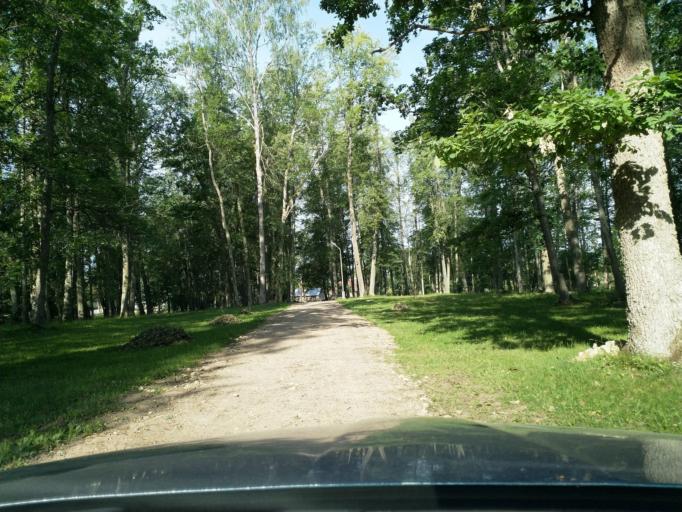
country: LV
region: Talsu Rajons
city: Sabile
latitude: 56.9520
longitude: 22.4019
